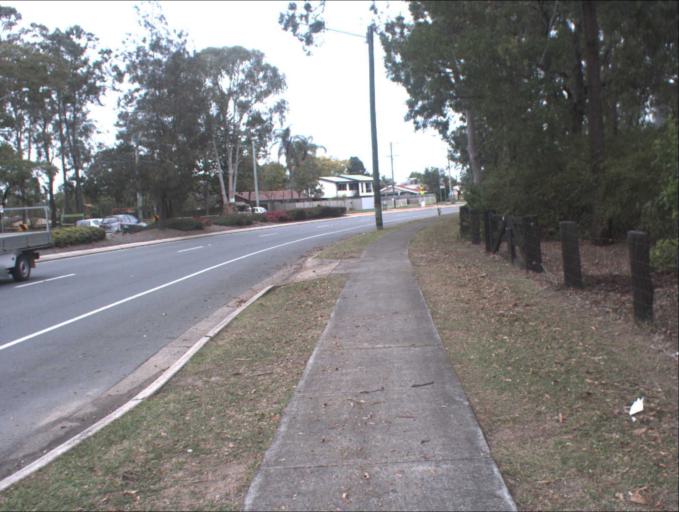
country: AU
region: Queensland
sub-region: Logan
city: Park Ridge South
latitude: -27.6844
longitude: 153.0170
